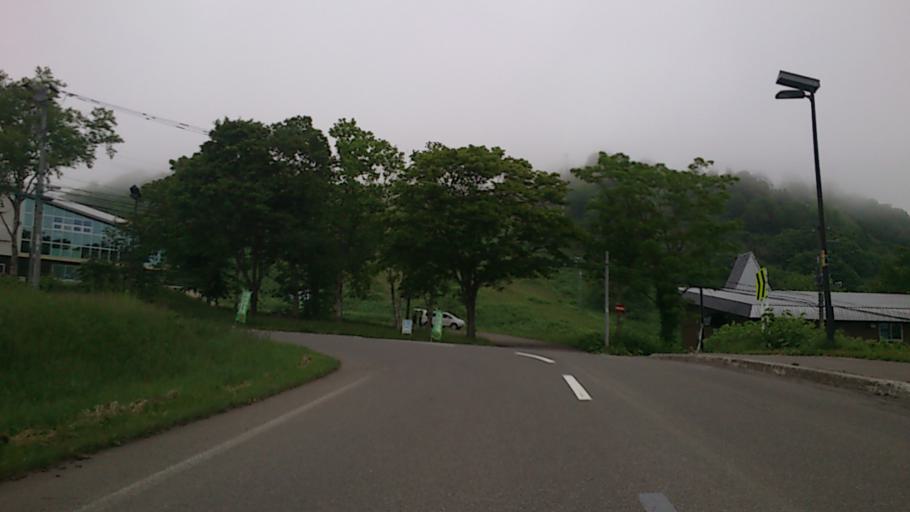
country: JP
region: Hokkaido
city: Niseko Town
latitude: 42.8482
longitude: 140.6451
